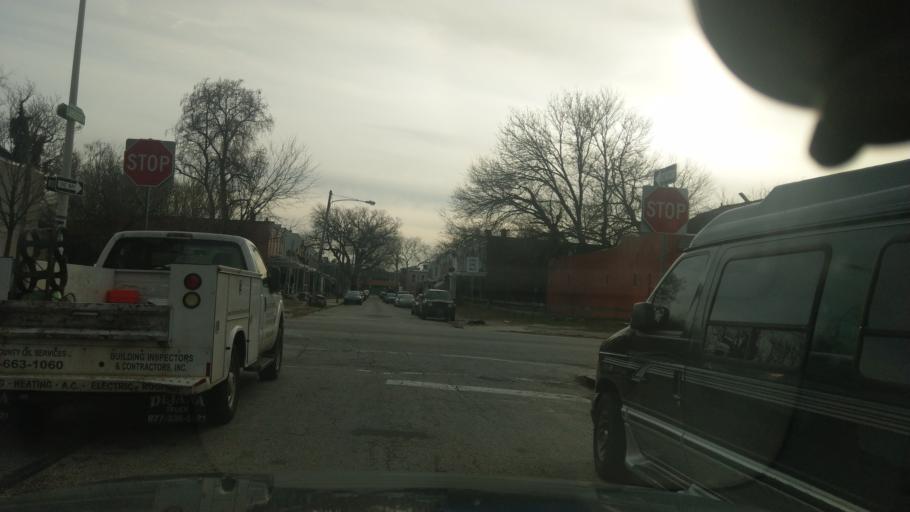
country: US
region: Pennsylvania
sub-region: Montgomery County
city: Wyncote
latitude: 40.0520
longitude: -75.1545
